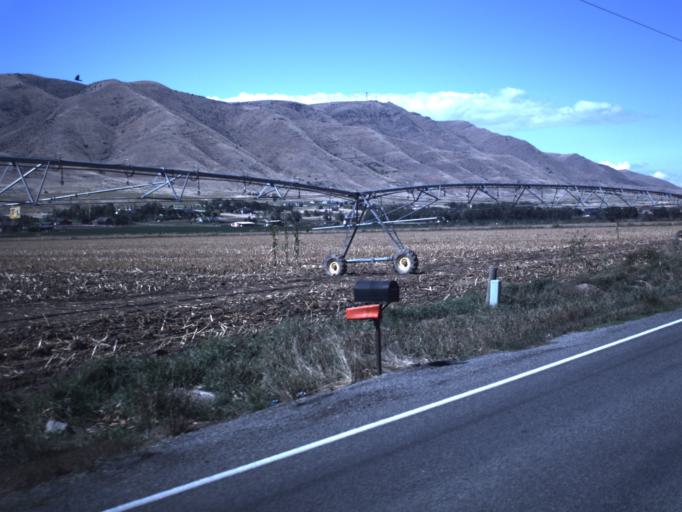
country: US
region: Utah
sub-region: Utah County
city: West Mountain
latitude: 40.0518
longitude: -111.7874
